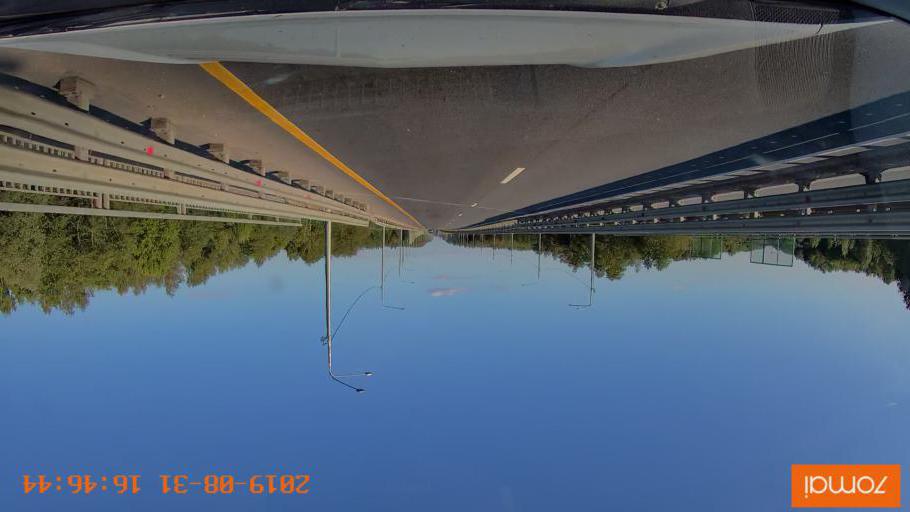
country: RU
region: Kaluga
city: Mstikhino
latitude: 54.6412
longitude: 36.1331
